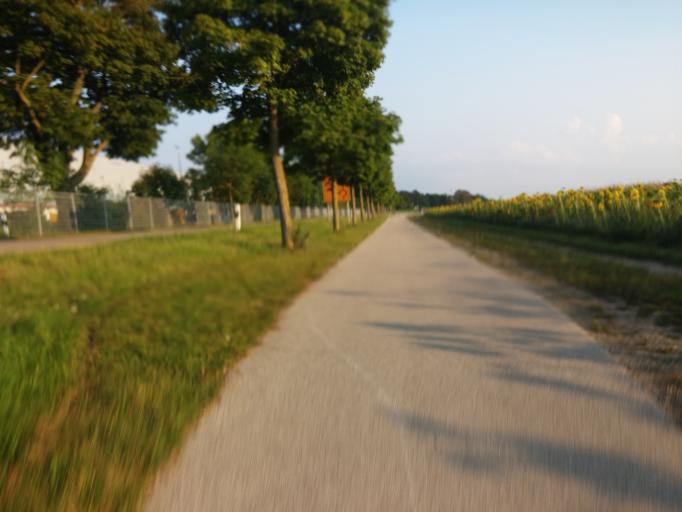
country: DE
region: Bavaria
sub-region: Upper Bavaria
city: Kirchheim bei Muenchen
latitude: 48.1622
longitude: 11.7832
